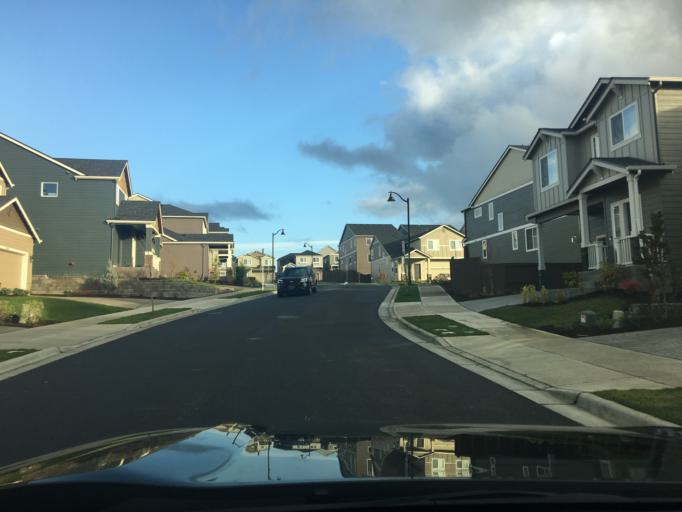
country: US
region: Oregon
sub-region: Washington County
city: Bethany
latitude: 45.5729
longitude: -122.8518
